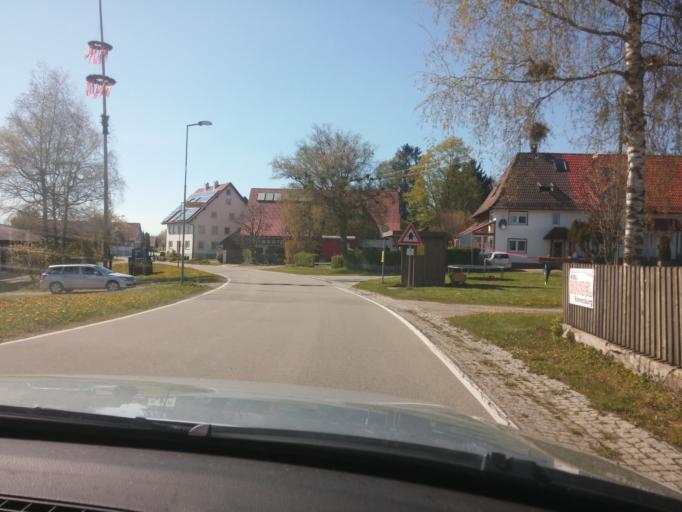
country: DE
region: Baden-Wuerttemberg
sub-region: Tuebingen Region
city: Bad Wurzach
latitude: 47.9451
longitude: 9.8898
